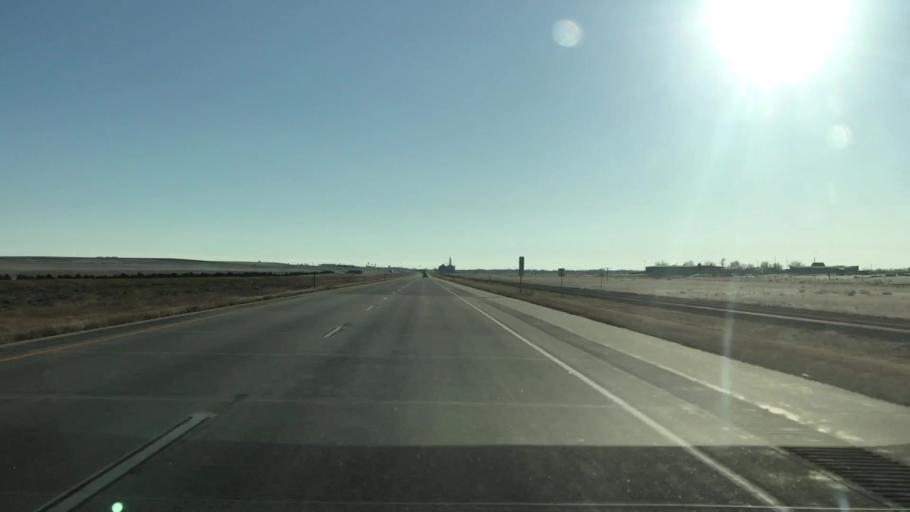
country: US
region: Colorado
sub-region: Lincoln County
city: Limon
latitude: 39.2768
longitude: -103.7531
